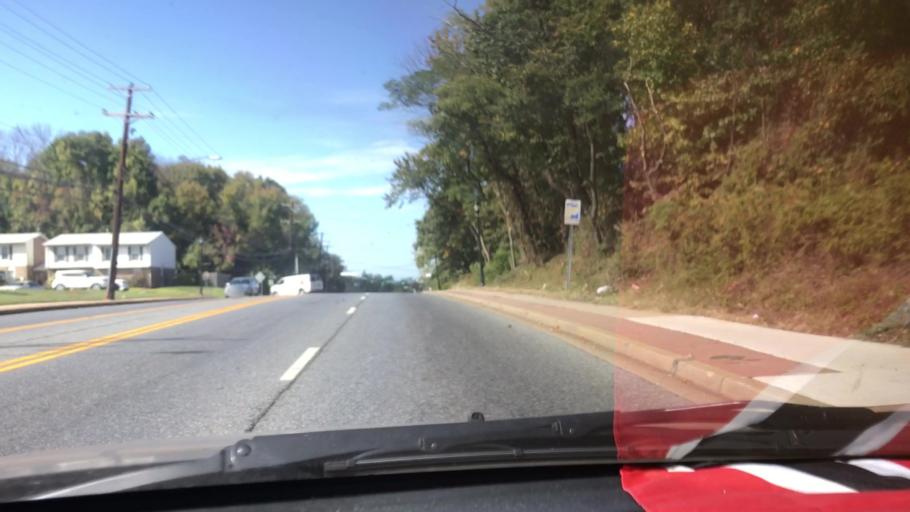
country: US
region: Maryland
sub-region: Prince George's County
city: Peppermill Village
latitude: 38.9129
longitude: -76.8794
